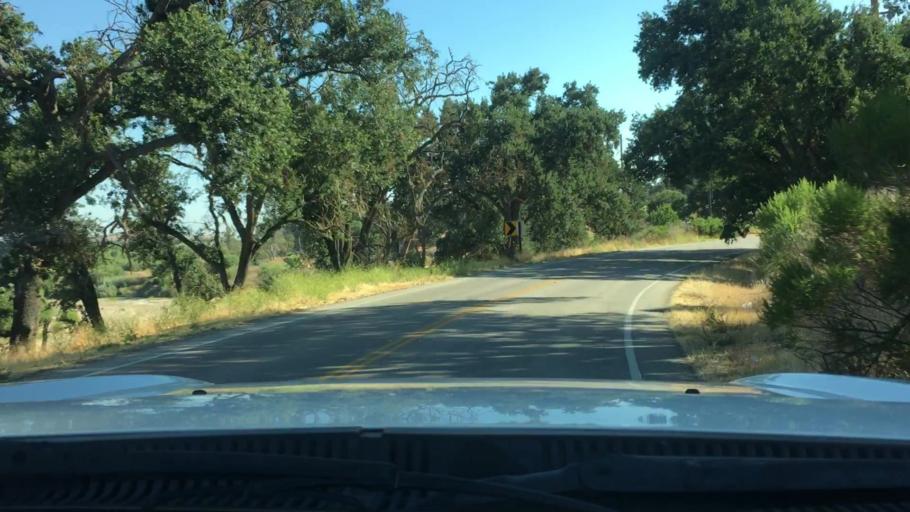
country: US
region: California
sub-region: San Luis Obispo County
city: Templeton
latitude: 35.5579
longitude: -120.6894
